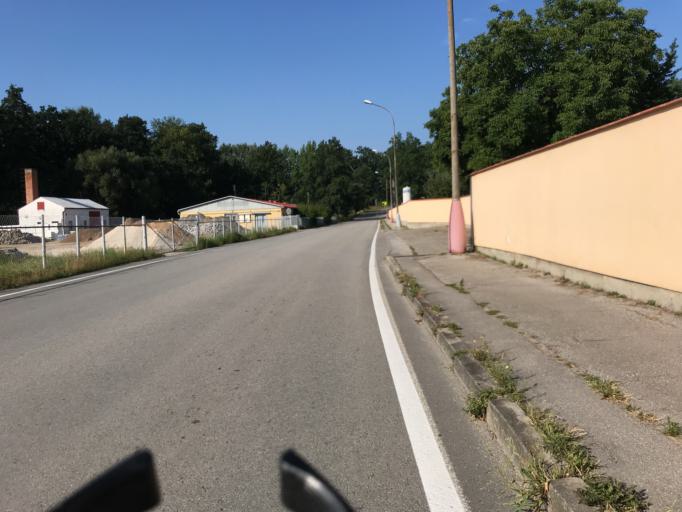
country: CZ
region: Jihocesky
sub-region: Okres Jindrichuv Hradec
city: Trebon
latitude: 48.9963
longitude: 14.7721
